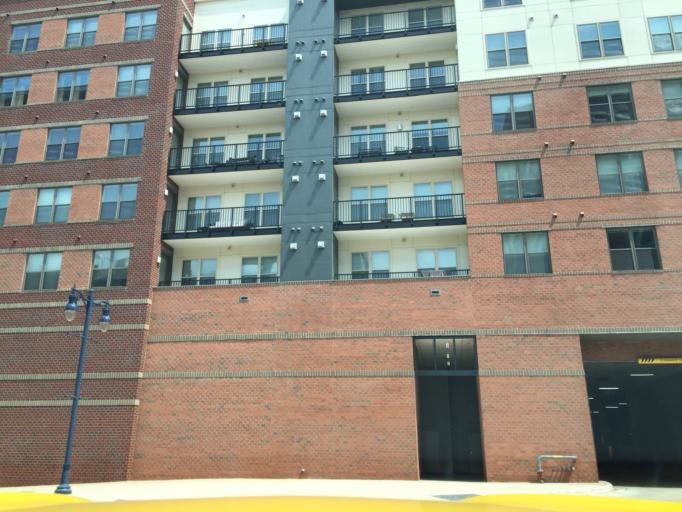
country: US
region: Maryland
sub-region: Prince George's County
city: Forest Heights
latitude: 38.7847
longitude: -77.0146
